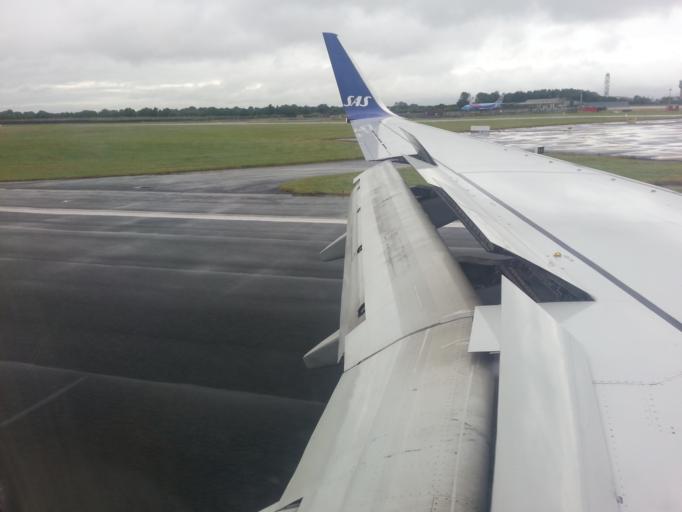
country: IE
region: Leinster
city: Ballymun
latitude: 53.4213
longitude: -6.2665
